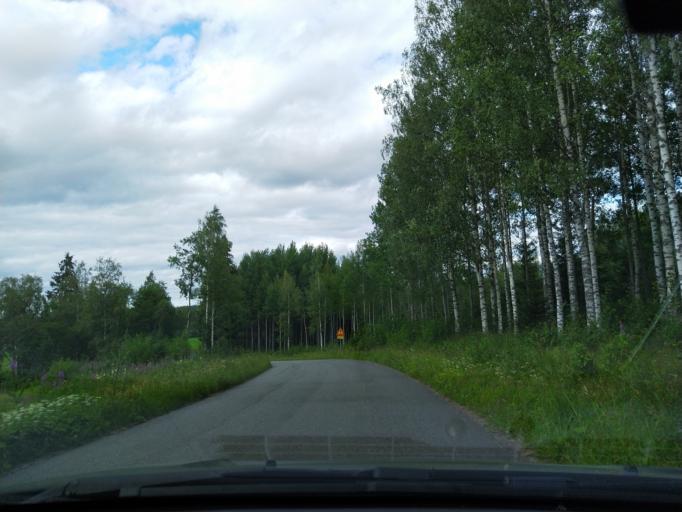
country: FI
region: Kymenlaakso
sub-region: Kouvola
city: Kouvola
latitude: 61.0481
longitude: 26.8462
